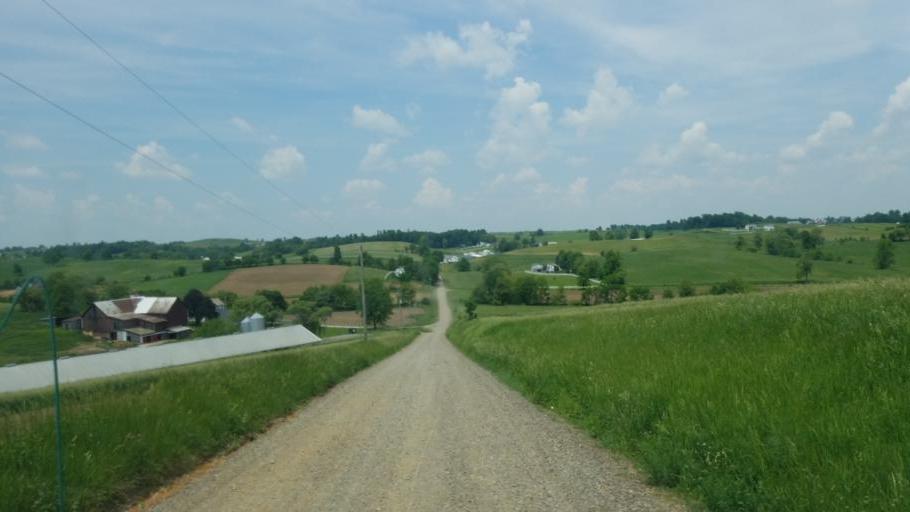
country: US
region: Ohio
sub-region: Tuscarawas County
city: Sugarcreek
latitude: 40.4698
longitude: -81.7563
